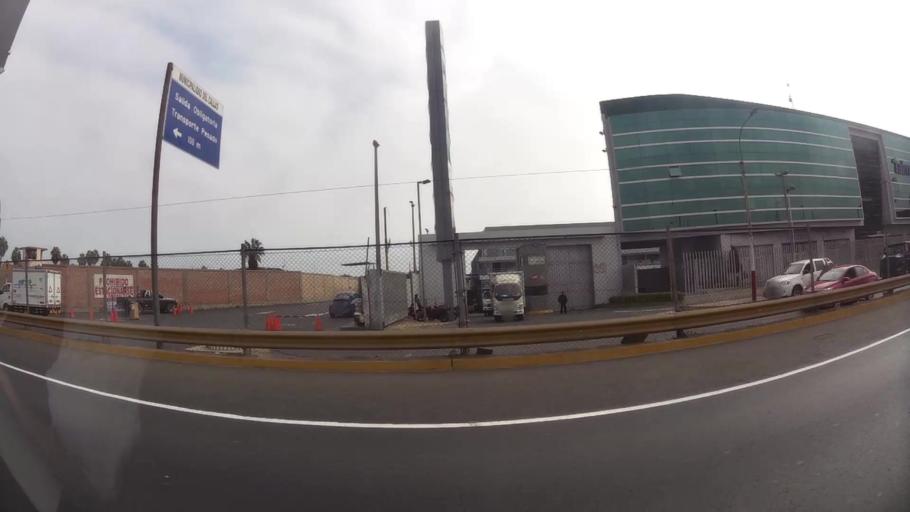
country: PE
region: Callao
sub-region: Callao
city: Callao
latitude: -12.0292
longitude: -77.1025
